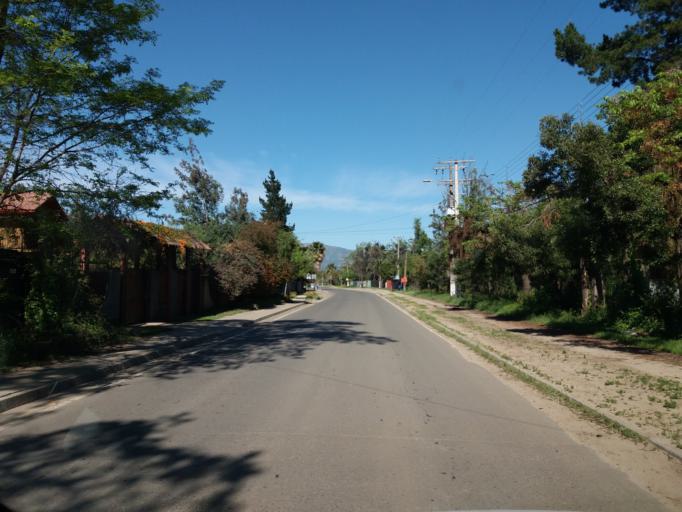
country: CL
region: Valparaiso
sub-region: Provincia de Marga Marga
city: Limache
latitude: -32.9929
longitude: -71.1677
